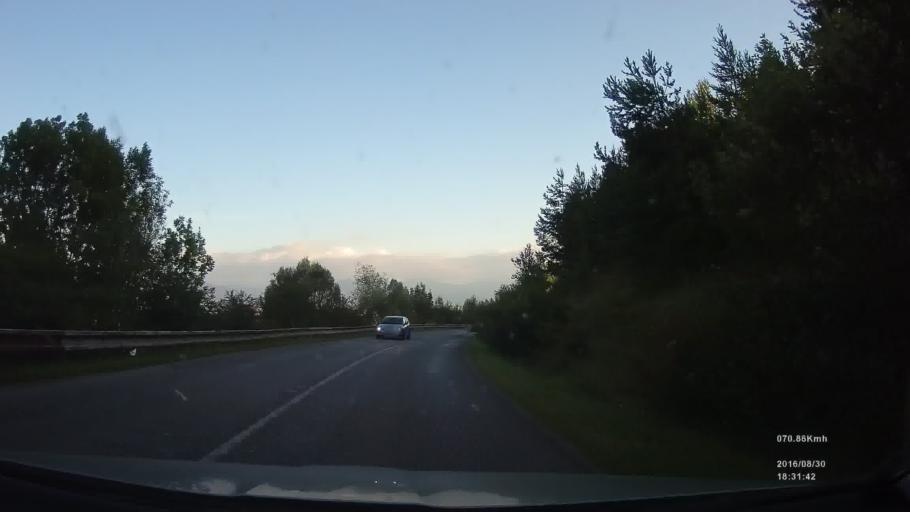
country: SK
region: Zilinsky
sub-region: Okres Liptovsky Mikulas
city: Liptovsky Mikulas
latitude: 49.1244
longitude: 19.5029
